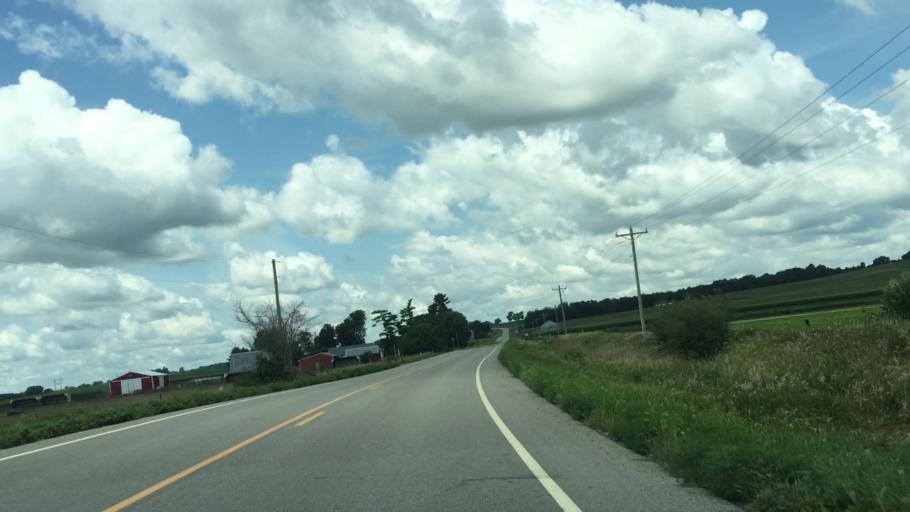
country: US
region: Iowa
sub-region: Linn County
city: Lisbon
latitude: 41.8408
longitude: -91.3993
